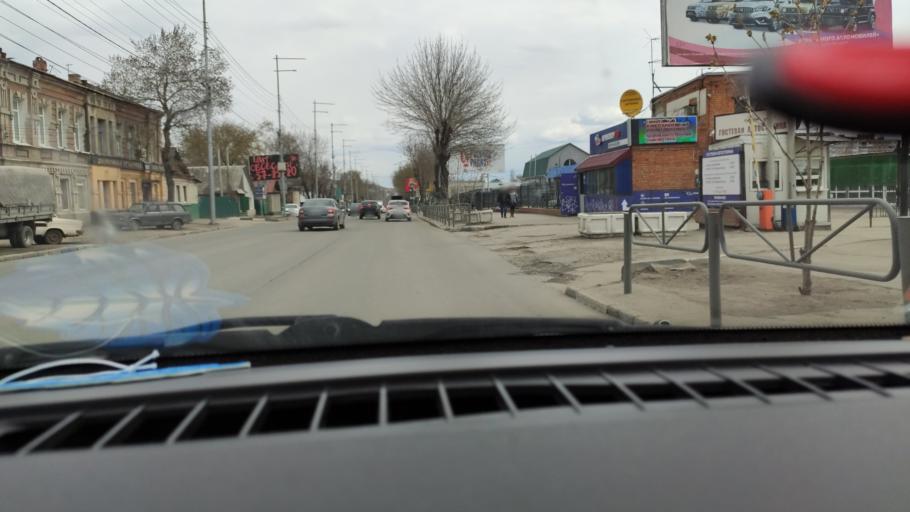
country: RU
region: Saratov
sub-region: Saratovskiy Rayon
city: Saratov
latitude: 51.5472
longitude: 46.0203
